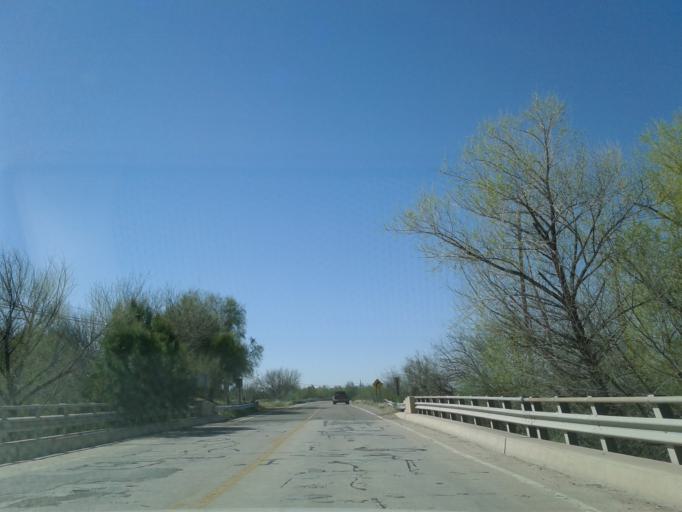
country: US
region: Arizona
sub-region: Pima County
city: Avra Valley
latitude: 32.4537
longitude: -111.2799
